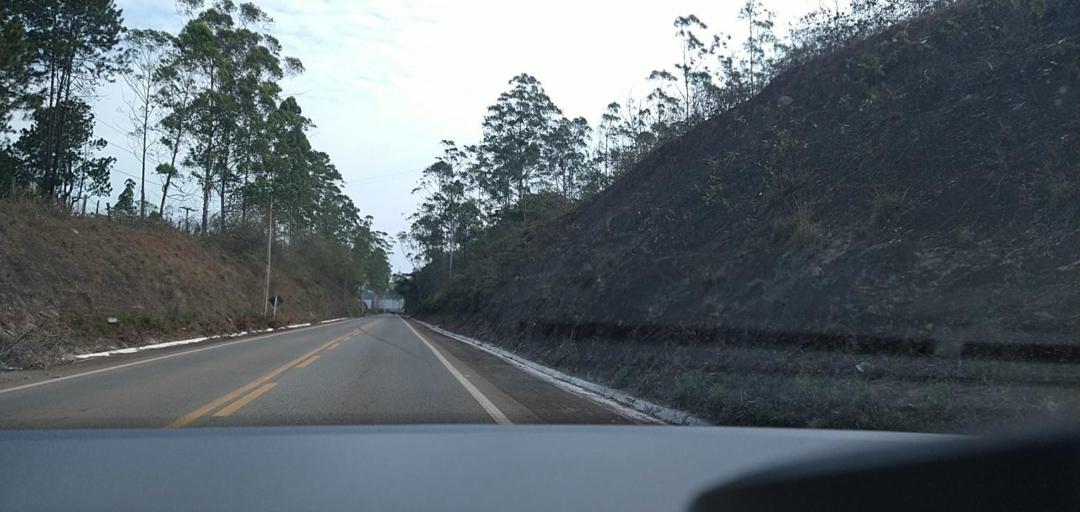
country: BR
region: Minas Gerais
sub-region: Rio Piracicaba
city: Rio Piracicaba
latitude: -19.8813
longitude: -43.1290
